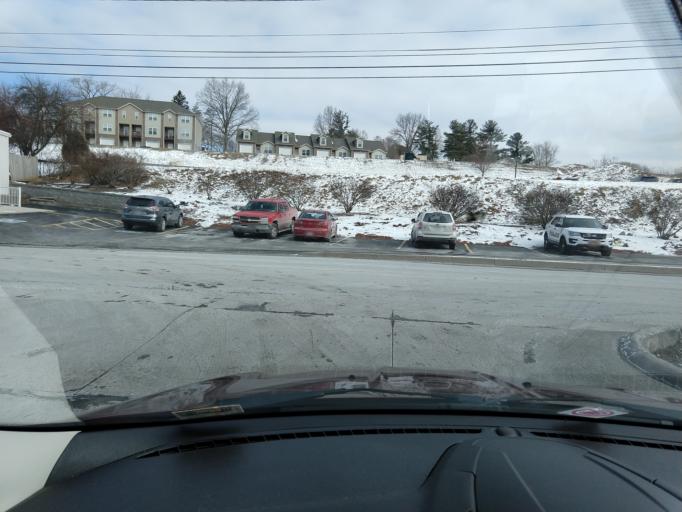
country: US
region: West Virginia
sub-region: Mercer County
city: Bluefield
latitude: 37.2444
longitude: -81.2399
